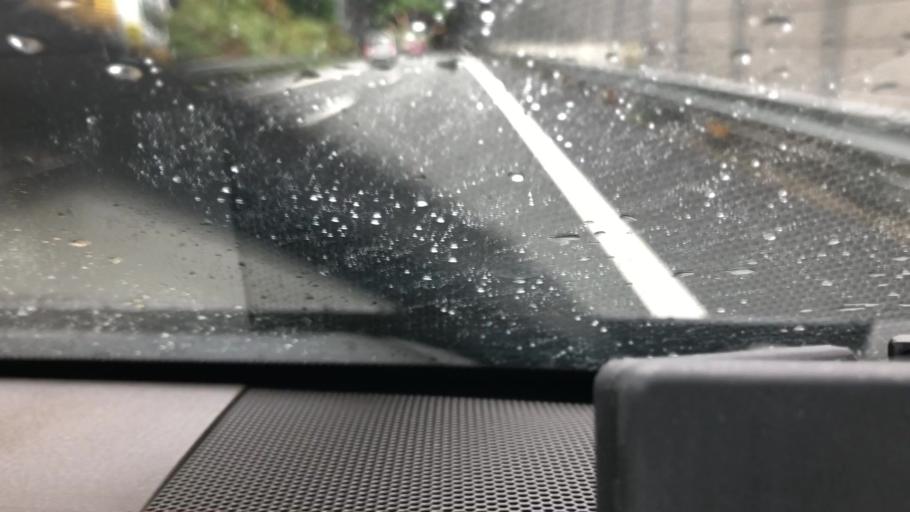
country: JP
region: Shizuoka
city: Mishima
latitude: 35.1975
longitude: 138.8887
